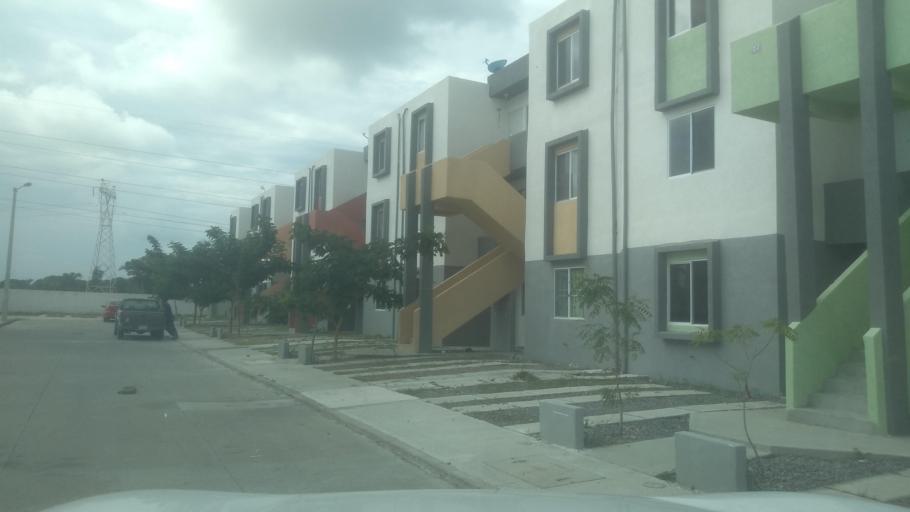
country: MX
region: Veracruz
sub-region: Medellin
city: Fraccionamiento Arboledas San Ramon
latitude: 19.0947
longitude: -96.1707
